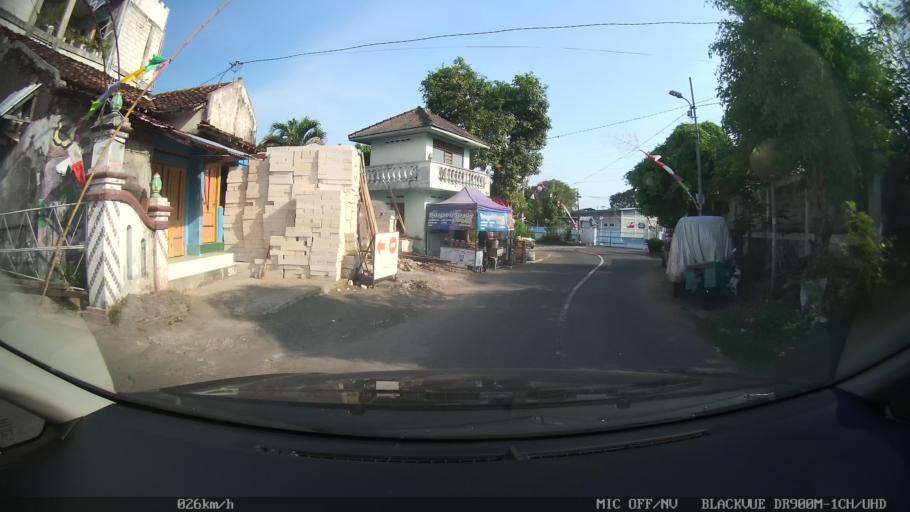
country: ID
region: Daerah Istimewa Yogyakarta
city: Yogyakarta
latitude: -7.8175
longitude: 110.3784
